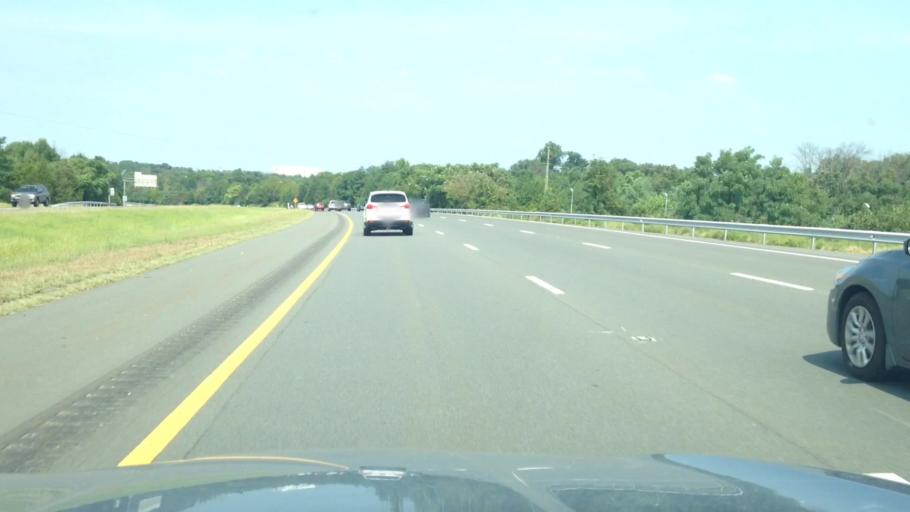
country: US
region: Virginia
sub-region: Loudoun County
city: Broadlands
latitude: 39.0312
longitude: -77.5090
